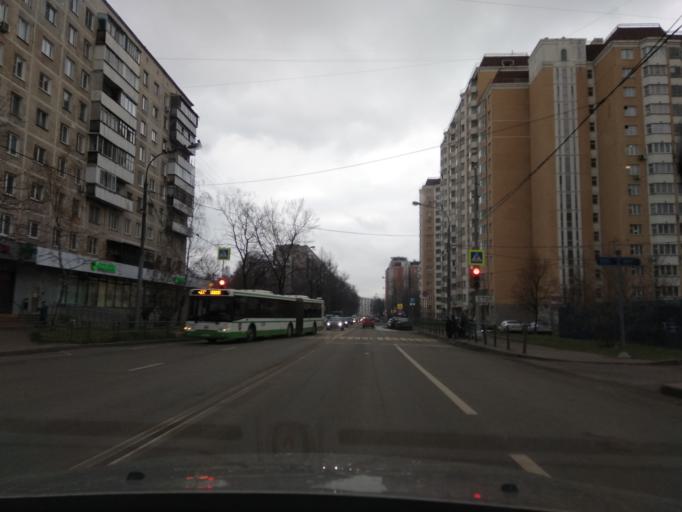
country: RU
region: Moskovskaya
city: Vostochnoe Degunino
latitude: 55.8685
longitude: 37.5626
